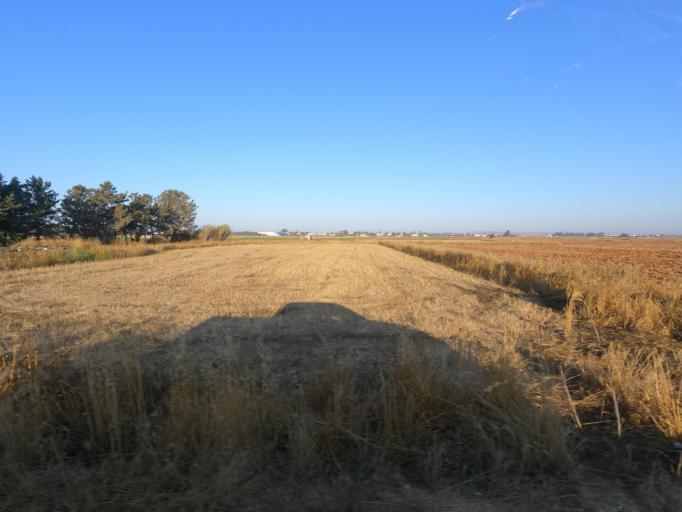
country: CY
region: Ammochostos
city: Achna
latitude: 35.0295
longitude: 33.7920
